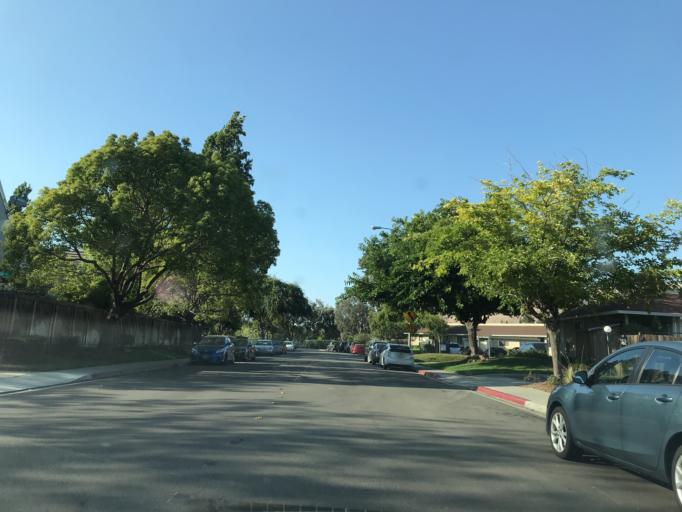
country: US
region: California
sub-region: Santa Clara County
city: Milpitas
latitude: 37.4406
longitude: -121.9152
